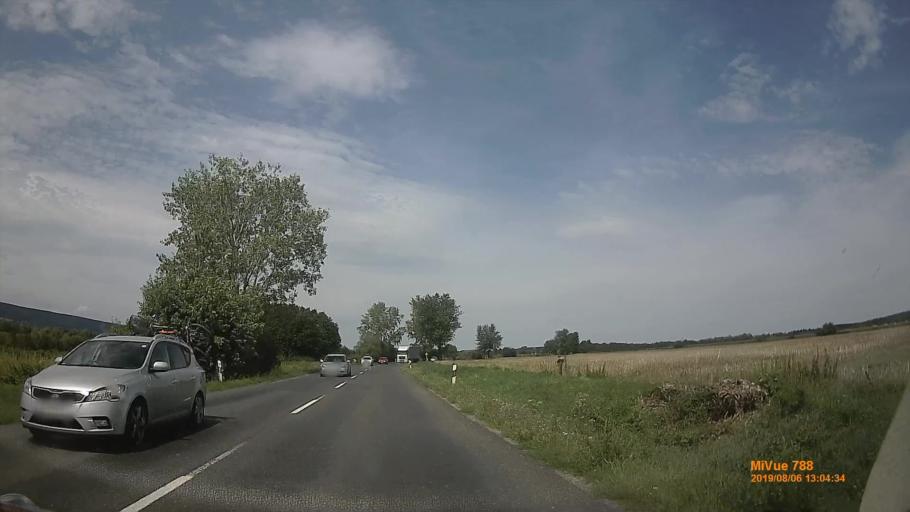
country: HU
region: Vas
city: Koszeg
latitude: 47.3543
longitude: 16.5683
